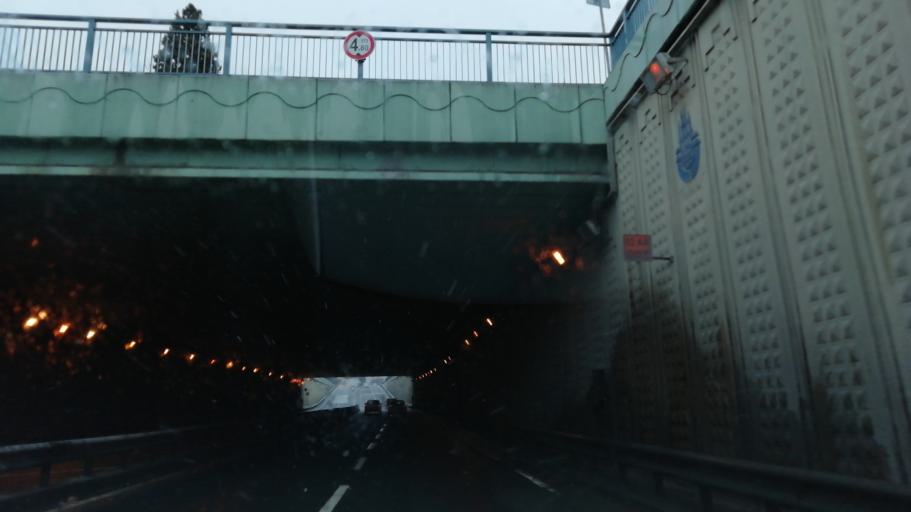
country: TR
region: Istanbul
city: Yakuplu
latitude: 40.9882
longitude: 28.7218
